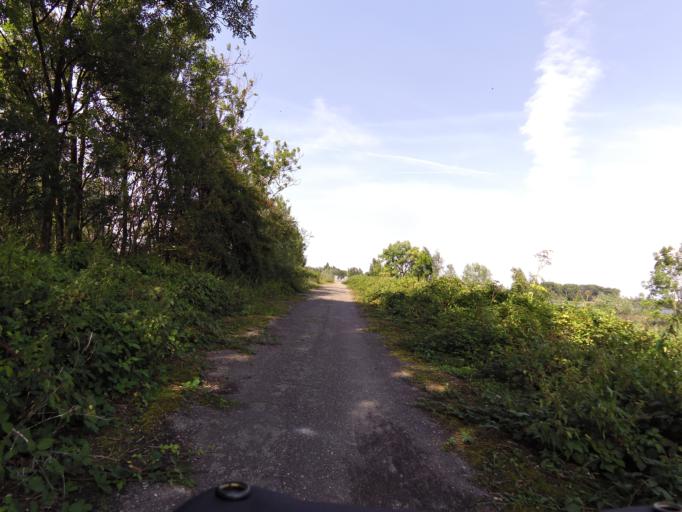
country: NL
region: South Holland
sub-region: Gemeente Barendrecht
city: Barendrecht
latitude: 51.8276
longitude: 4.5267
